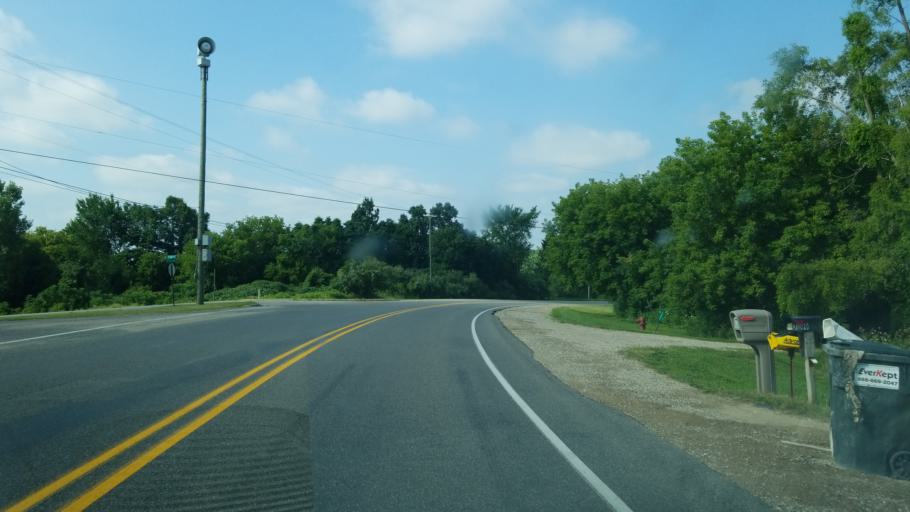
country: US
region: Michigan
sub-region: Kent County
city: Northview
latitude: 43.0914
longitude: -85.6391
